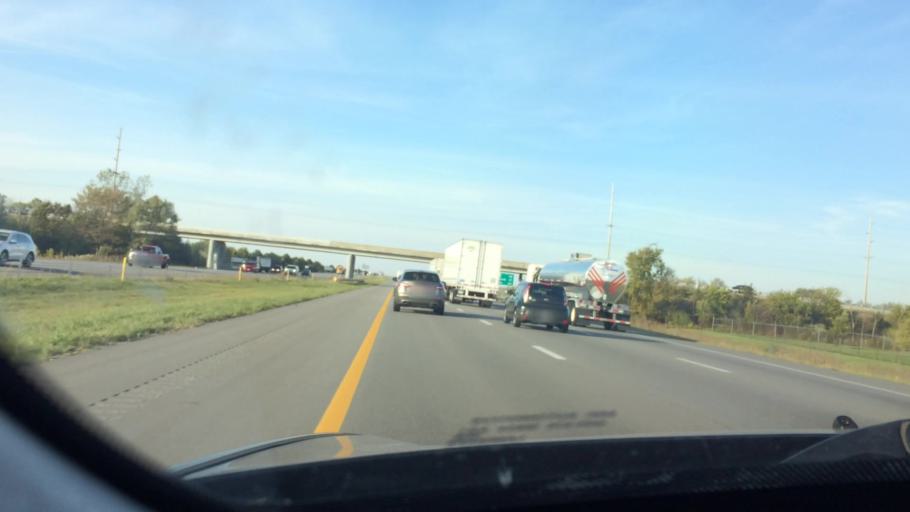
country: US
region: Ohio
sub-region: Wood County
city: Bowling Green
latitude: 41.3838
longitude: -83.6159
